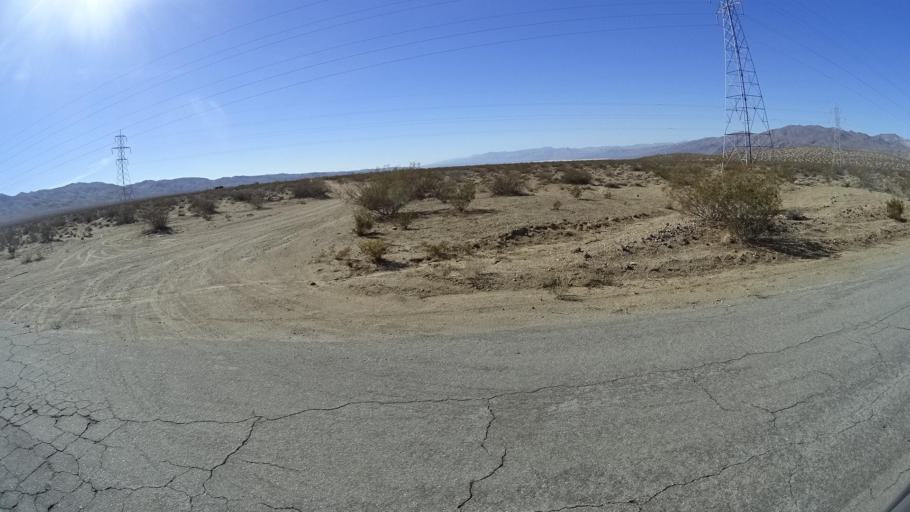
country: US
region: California
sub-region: Kern County
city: Ridgecrest
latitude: 35.4089
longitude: -117.6830
